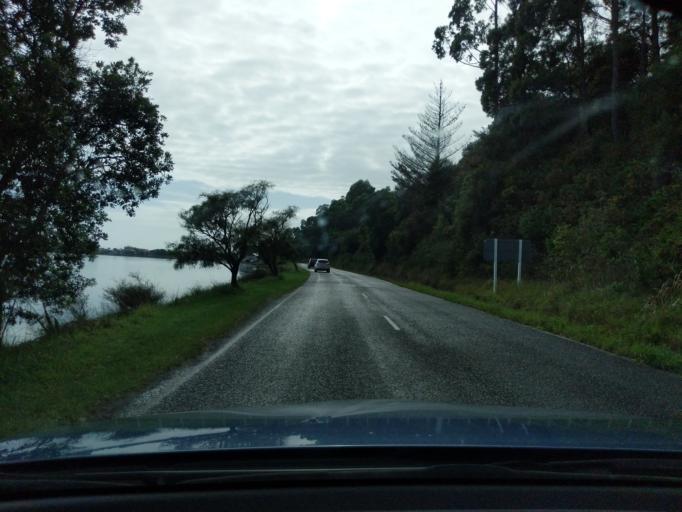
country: NZ
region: Tasman
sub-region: Tasman District
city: Takaka
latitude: -40.6807
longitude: 172.6753
